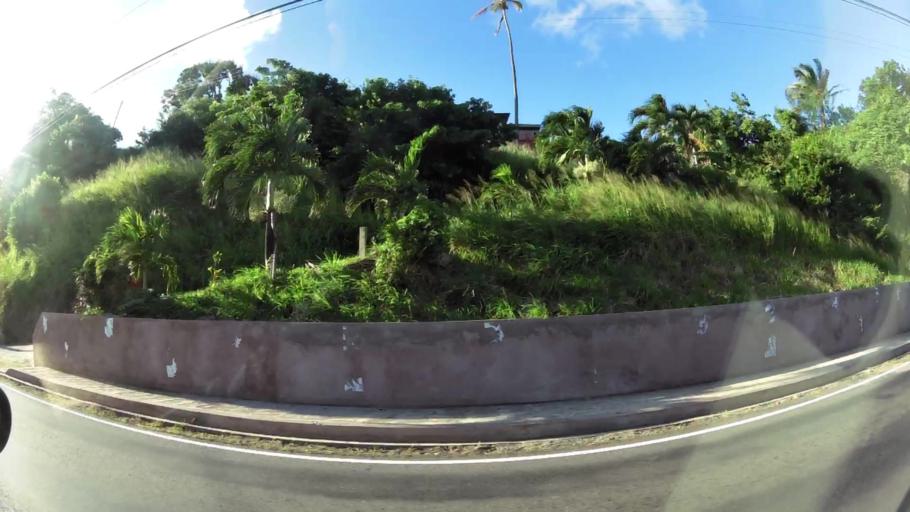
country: TT
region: Tobago
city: Scarborough
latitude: 11.1816
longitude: -60.7033
